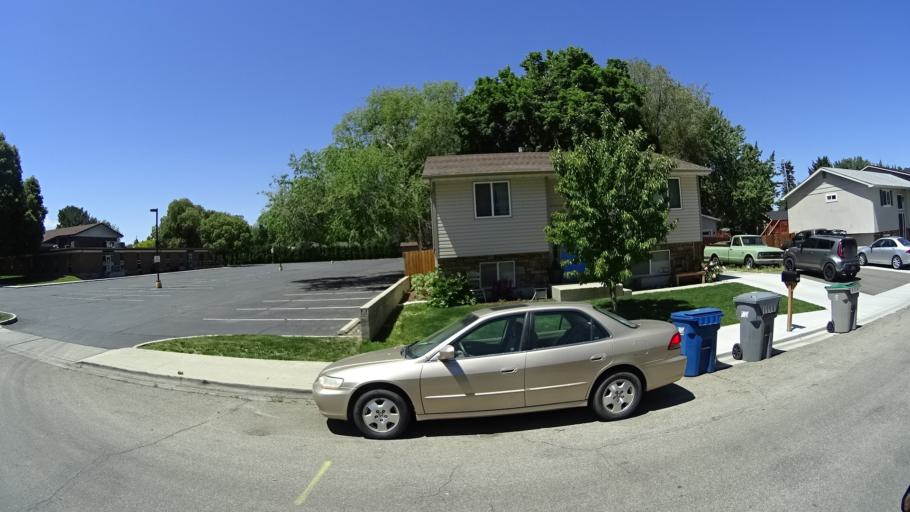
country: US
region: Idaho
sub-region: Ada County
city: Boise
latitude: 43.5819
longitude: -116.2186
